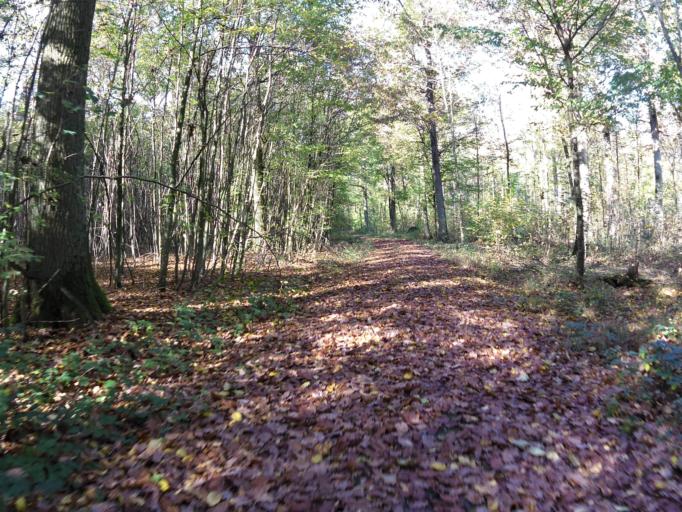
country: DE
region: Bavaria
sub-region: Regierungsbezirk Unterfranken
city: Sulzfeld am Main
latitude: 49.7200
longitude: 10.0939
